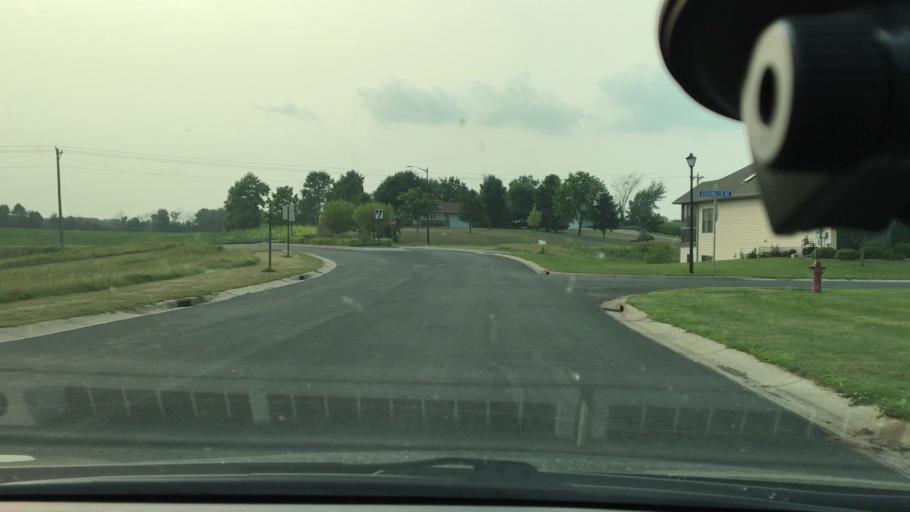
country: US
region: Minnesota
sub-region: Wright County
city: Albertville
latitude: 45.2851
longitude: -93.6828
